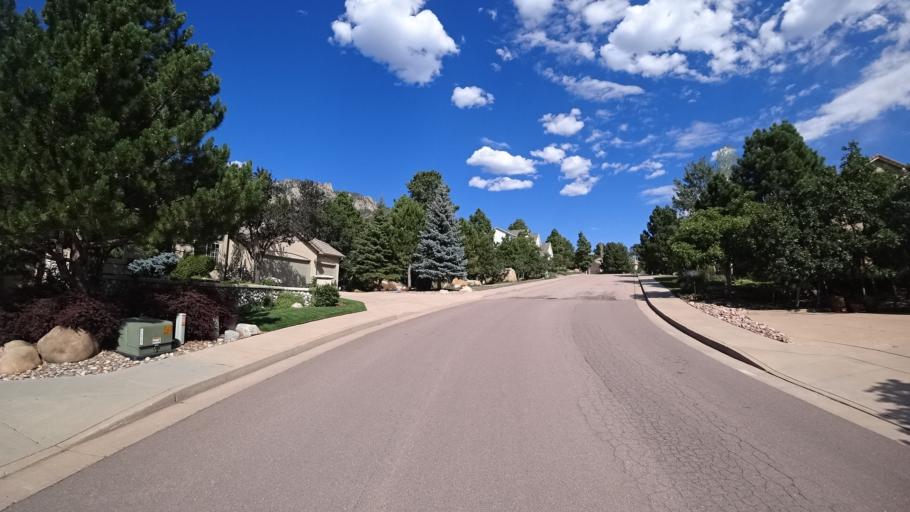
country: US
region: Colorado
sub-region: El Paso County
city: Fort Carson
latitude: 38.7535
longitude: -104.8359
